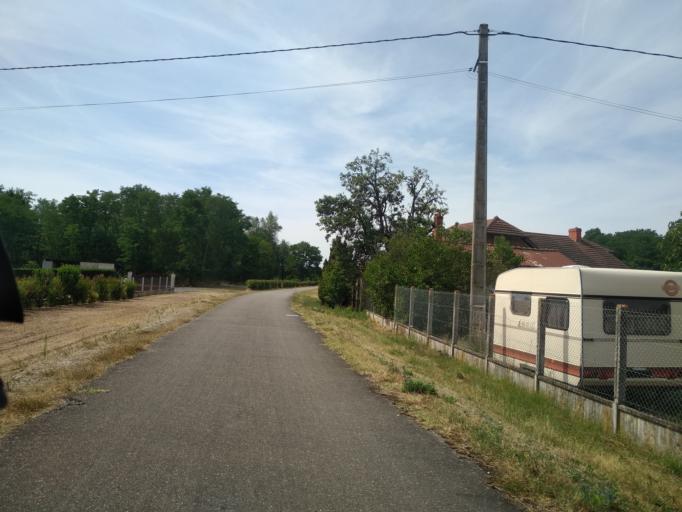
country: FR
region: Auvergne
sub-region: Departement de l'Allier
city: Diou
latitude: 46.5399
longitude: 3.7507
